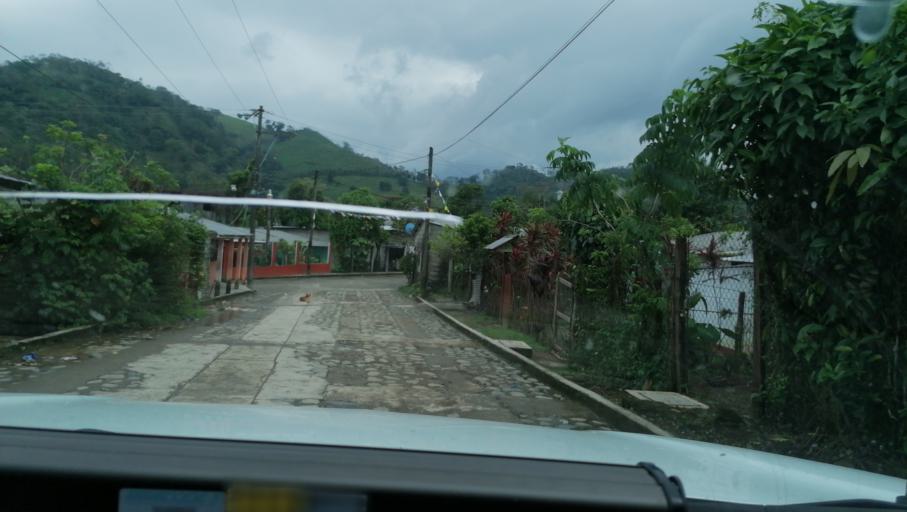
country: MX
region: Chiapas
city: Ixtacomitan
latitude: 17.3431
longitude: -93.1322
